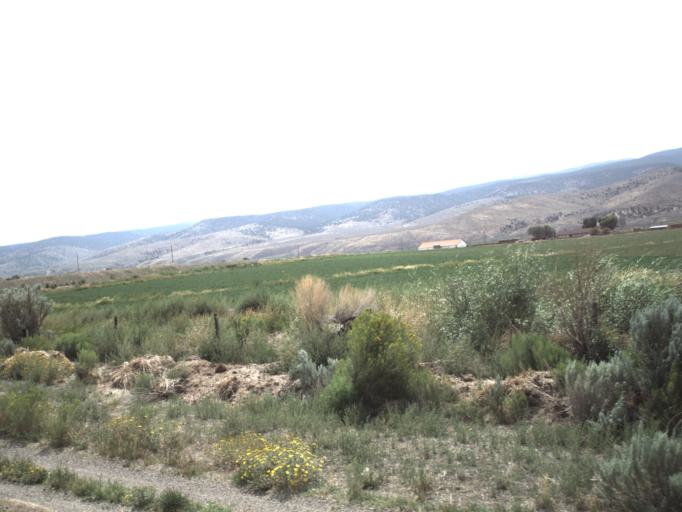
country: US
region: Utah
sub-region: Piute County
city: Junction
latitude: 38.1413
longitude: -111.9980
